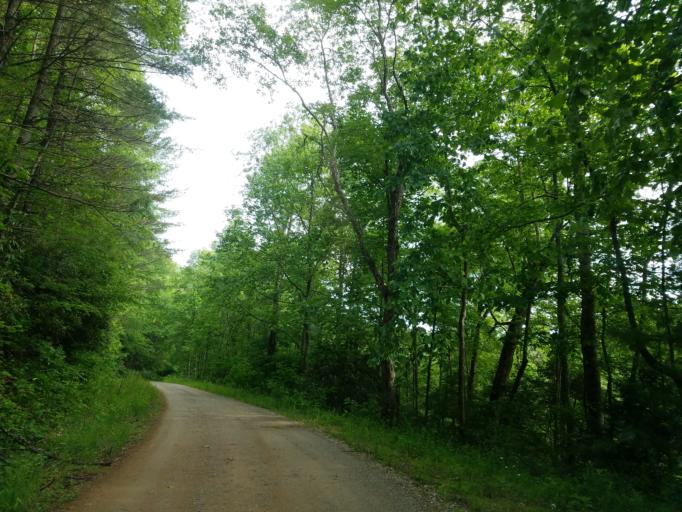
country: US
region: Georgia
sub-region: Union County
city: Blairsville
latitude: 34.7572
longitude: -84.0126
